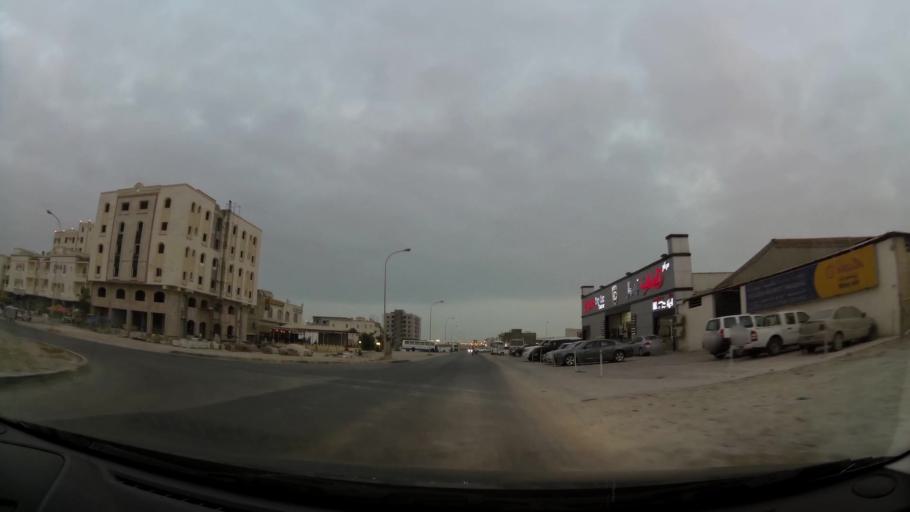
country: OM
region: Zufar
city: Salalah
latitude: 17.0264
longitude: 54.0537
